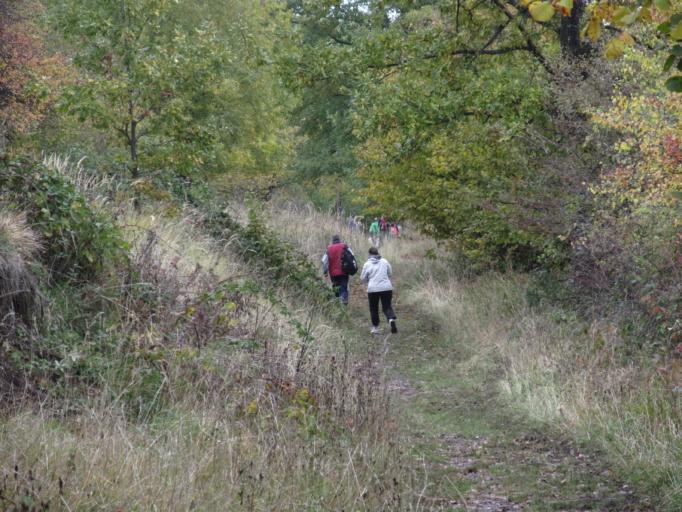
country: HU
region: Nograd
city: Batonyterenye
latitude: 47.9258
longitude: 19.8598
